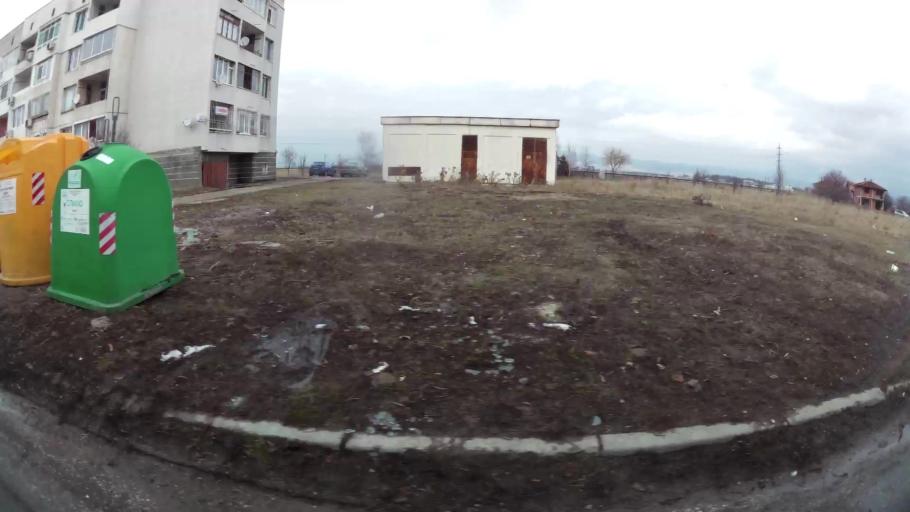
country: BG
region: Sofiya
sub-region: Obshtina Bozhurishte
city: Bozhurishte
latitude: 42.7455
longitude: 23.2643
